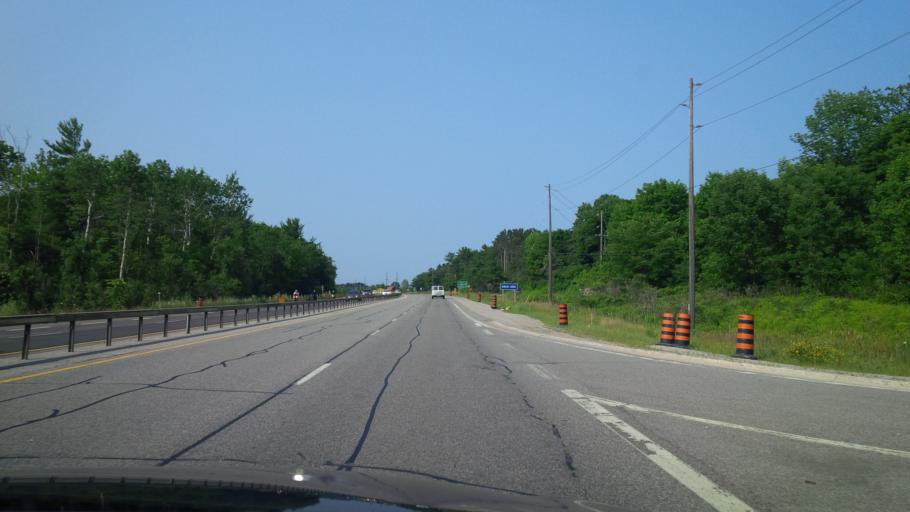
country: CA
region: Ontario
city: Orillia
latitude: 44.7284
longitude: -79.3697
